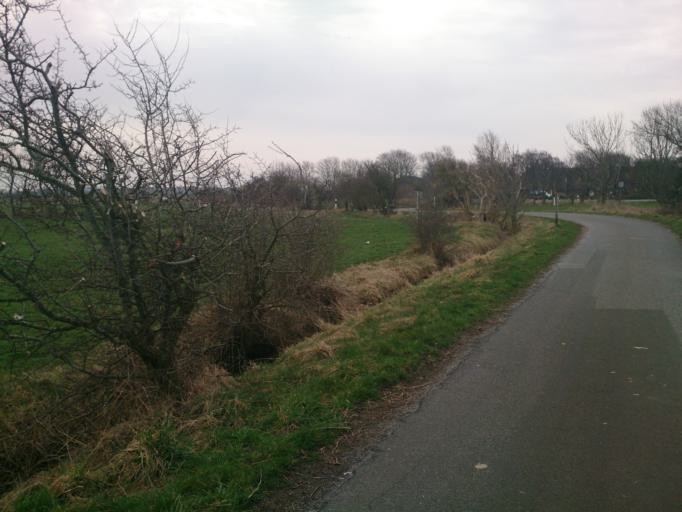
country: DE
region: Schleswig-Holstein
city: Utersum
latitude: 54.7169
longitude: 8.4078
